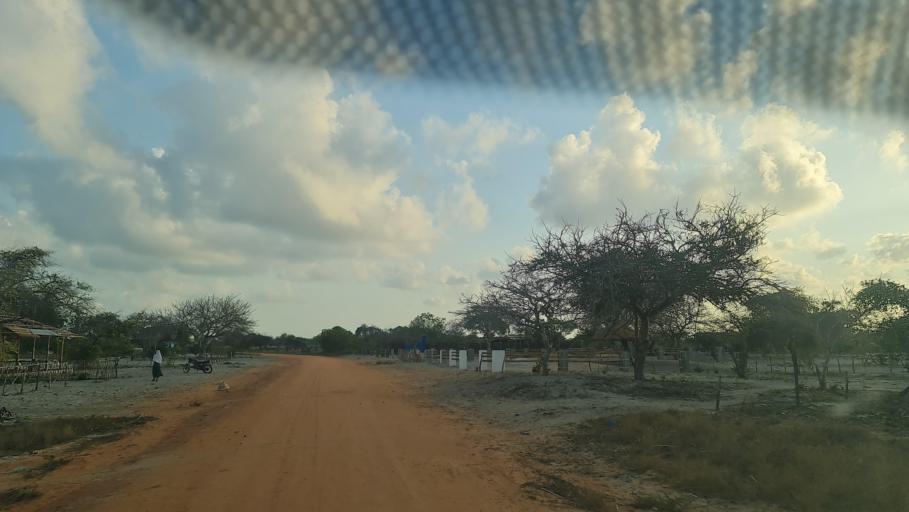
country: MZ
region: Nampula
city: Nacala
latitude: -14.7809
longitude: 40.8211
